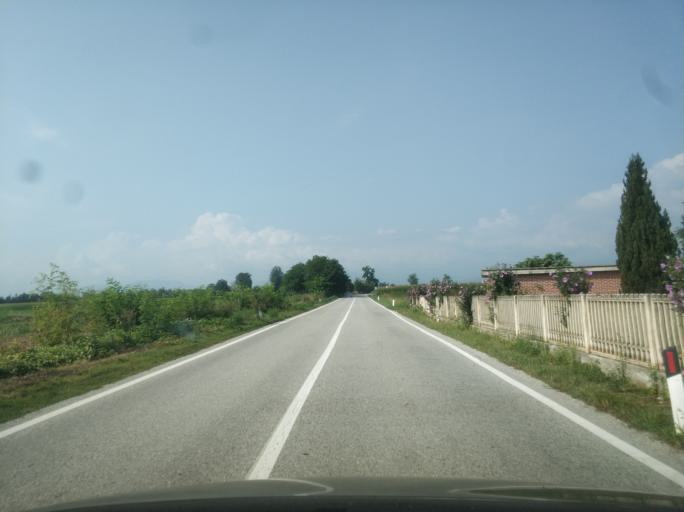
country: IT
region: Piedmont
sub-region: Provincia di Cuneo
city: Tarantasca
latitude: 44.4815
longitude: 7.5365
